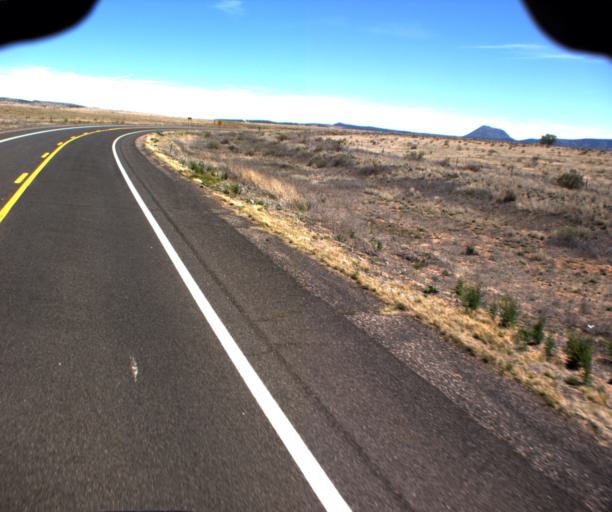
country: US
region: Arizona
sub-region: Yavapai County
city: Paulden
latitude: 35.3232
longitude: -112.8522
